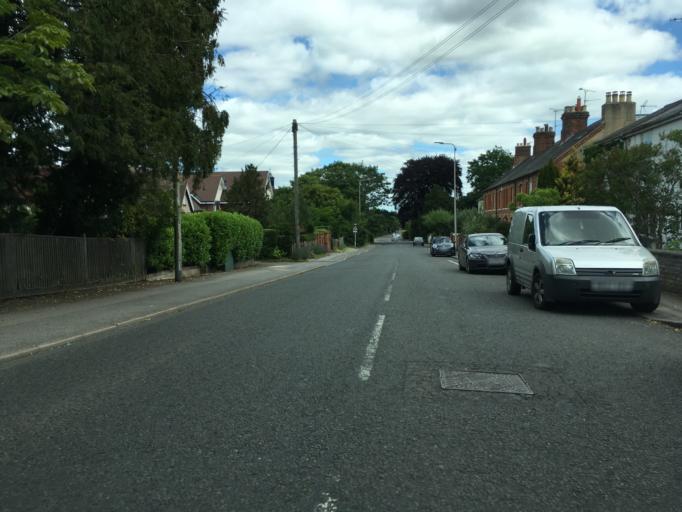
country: GB
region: England
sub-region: West Berkshire
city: Newbury
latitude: 51.3906
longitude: -1.3317
